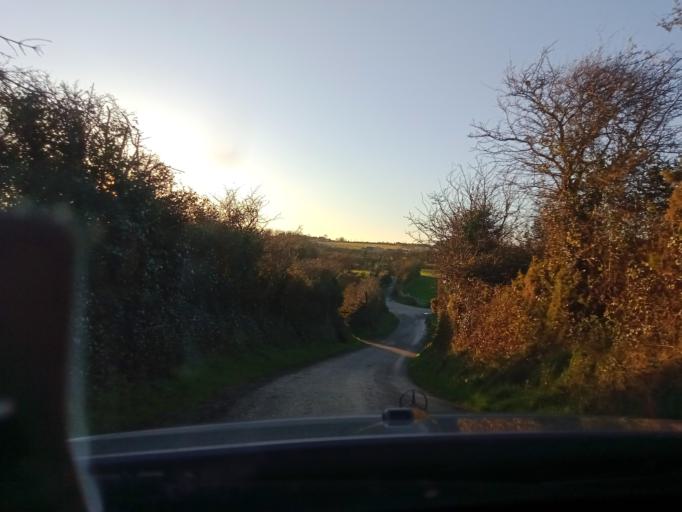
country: IE
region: Leinster
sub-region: Loch Garman
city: New Ross
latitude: 52.3744
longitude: -7.0166
